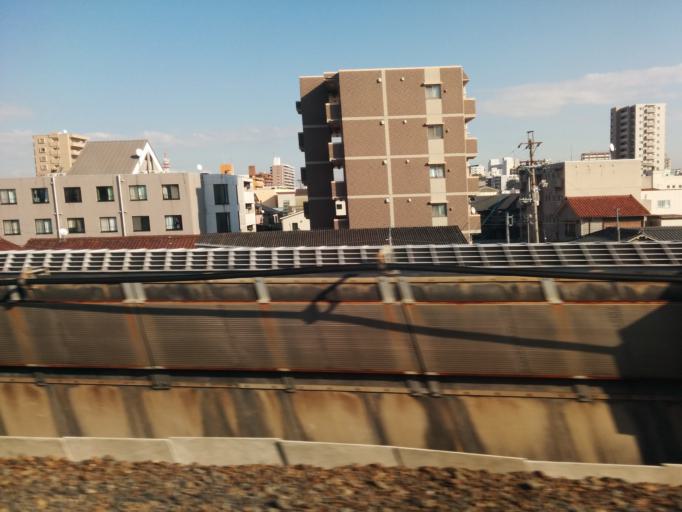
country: JP
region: Aichi
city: Nagoya-shi
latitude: 35.1331
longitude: 136.8856
